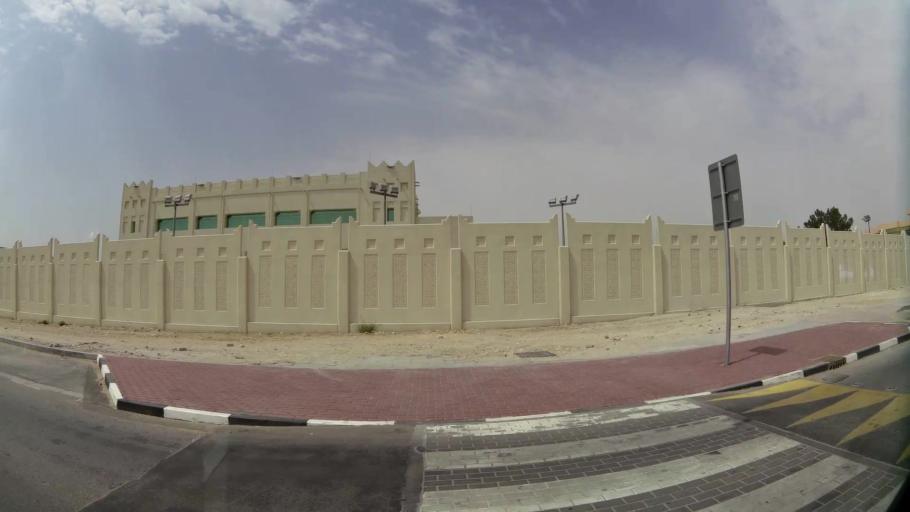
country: QA
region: Baladiyat ad Dawhah
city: Doha
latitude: 25.3094
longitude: 51.4766
